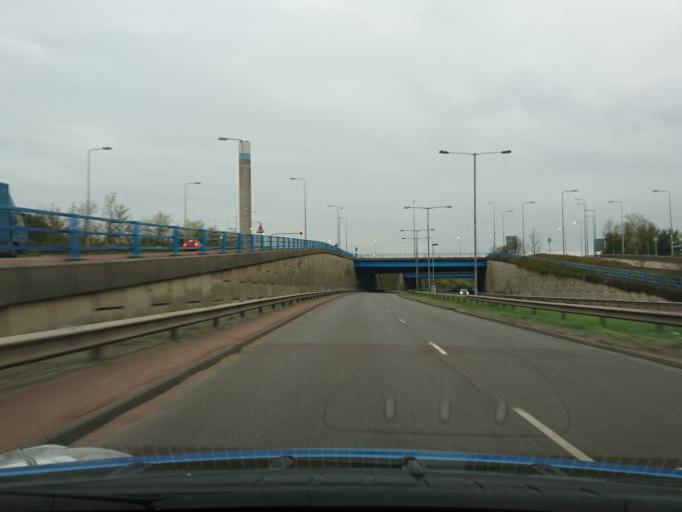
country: GB
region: England
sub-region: Stoke-on-Trent
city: Stoke-on-Trent
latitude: 52.9924
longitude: -2.1824
